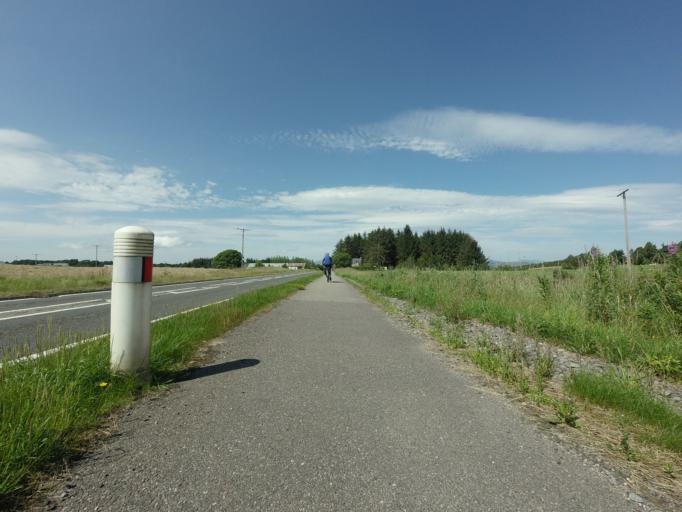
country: GB
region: Scotland
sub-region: Highland
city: Conon Bridge
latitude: 57.5454
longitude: -4.3843
